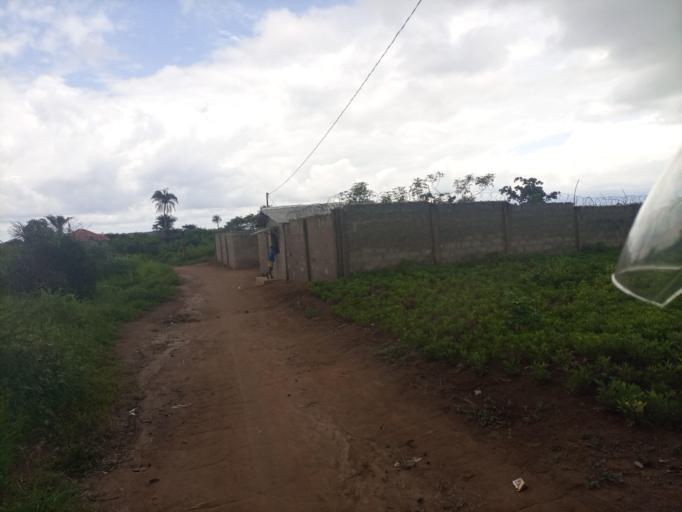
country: SL
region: Northern Province
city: Masoyila
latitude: 8.5786
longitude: -13.1589
